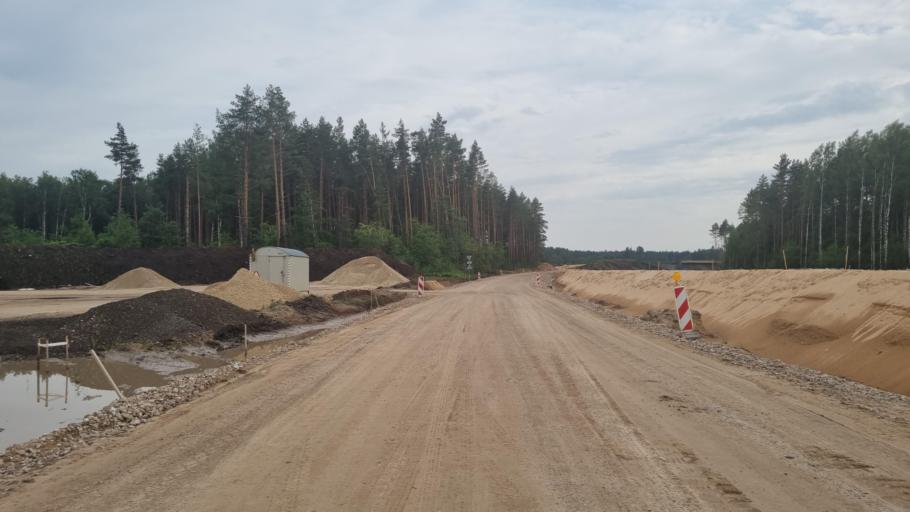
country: LV
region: Kekava
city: Balozi
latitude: 56.8709
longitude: 24.1682
